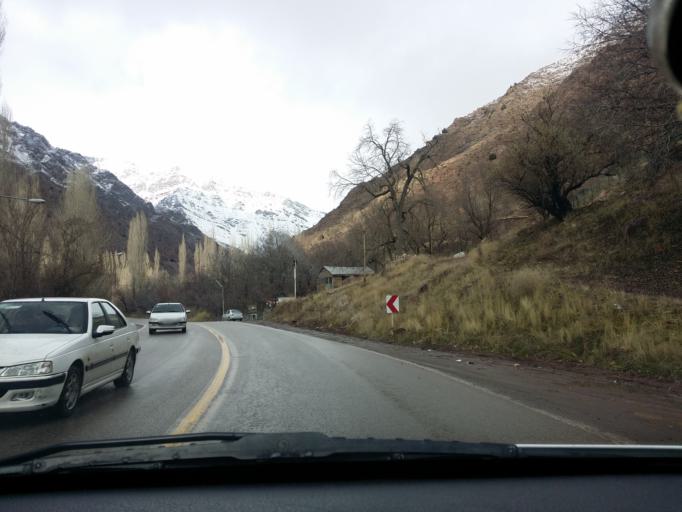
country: IR
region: Tehran
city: Tajrish
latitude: 36.0540
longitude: 51.3138
